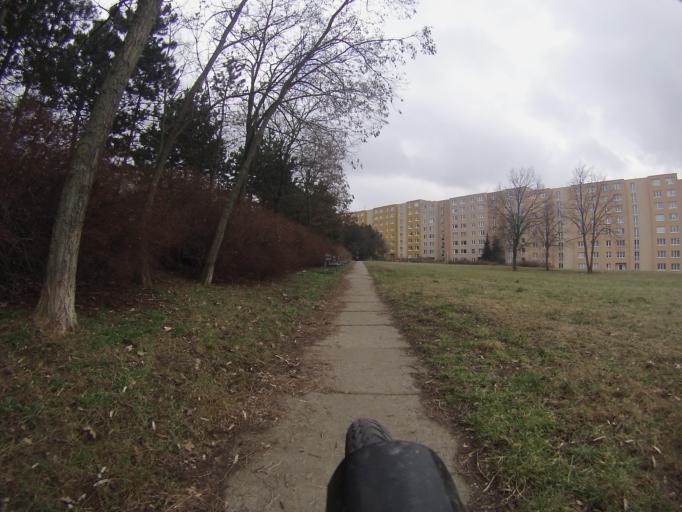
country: CZ
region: South Moravian
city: Bilovice nad Svitavou
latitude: 49.2106
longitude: 16.6763
